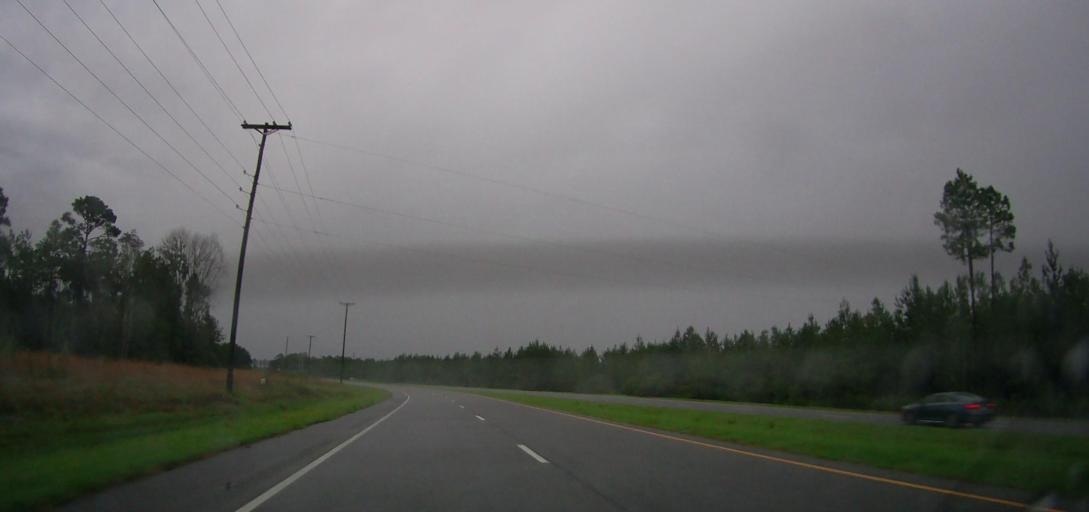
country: US
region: Georgia
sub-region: Clinch County
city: Homerville
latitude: 31.0142
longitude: -82.8224
